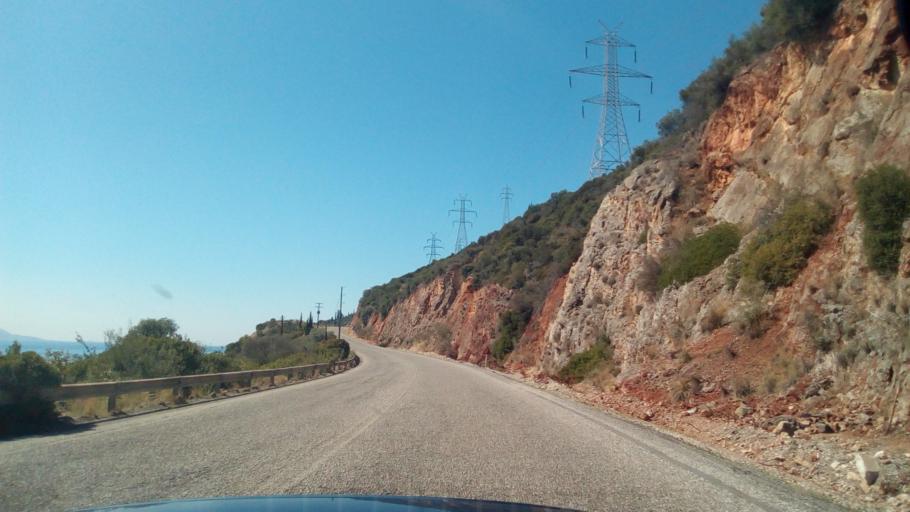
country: GR
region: West Greece
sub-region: Nomos Achaias
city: Kamarai
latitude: 38.3953
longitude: 22.0522
